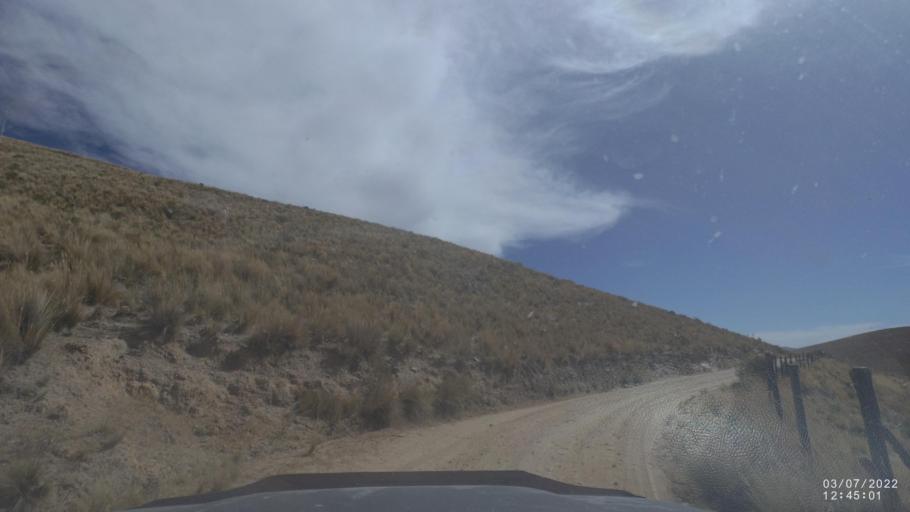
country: BO
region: Cochabamba
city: Irpa Irpa
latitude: -17.7794
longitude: -66.6343
